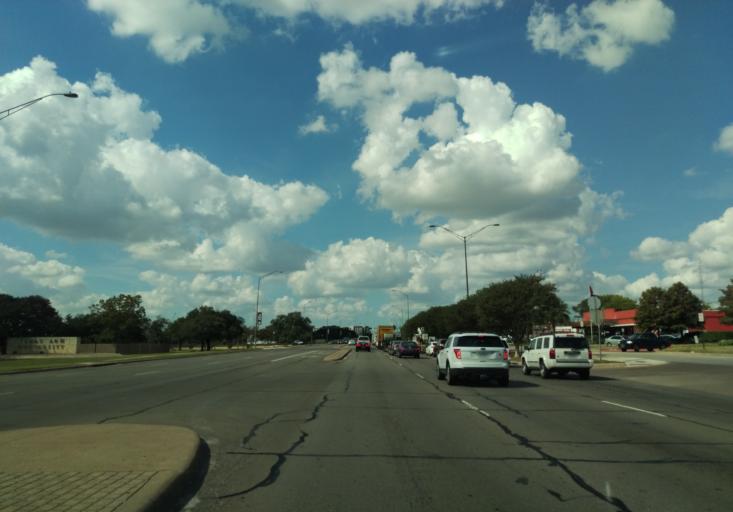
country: US
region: Texas
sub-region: Brazos County
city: College Station
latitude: 30.6220
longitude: -96.3279
